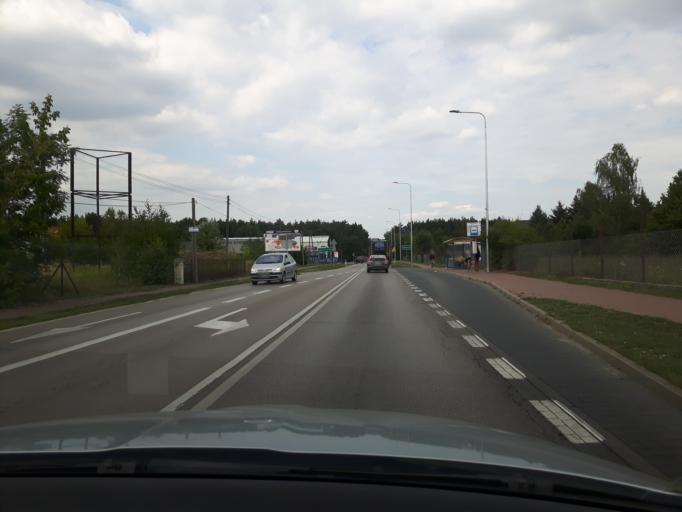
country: PL
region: Masovian Voivodeship
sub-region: Powiat legionowski
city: Stanislawow Pierwszy
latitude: 52.3977
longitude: 21.0355
